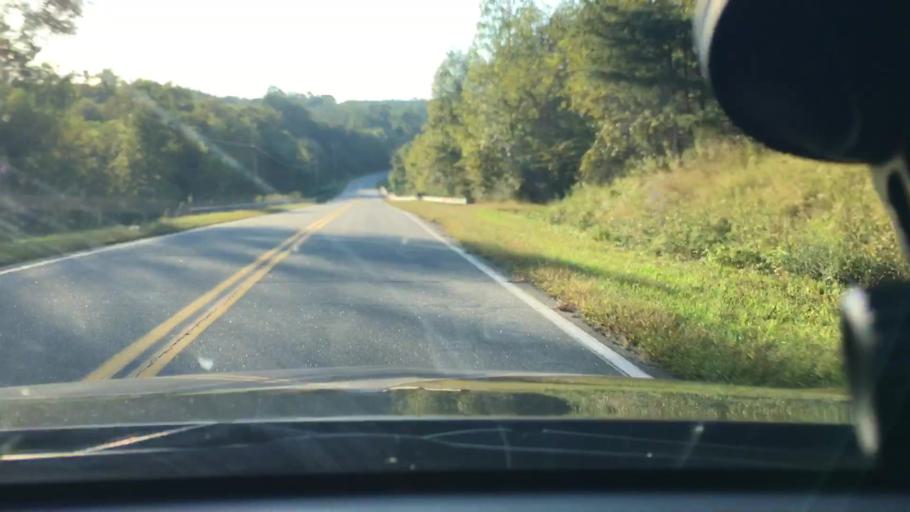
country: US
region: North Carolina
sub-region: Rutherford County
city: Rutherfordton
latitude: 35.3308
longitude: -82.0298
